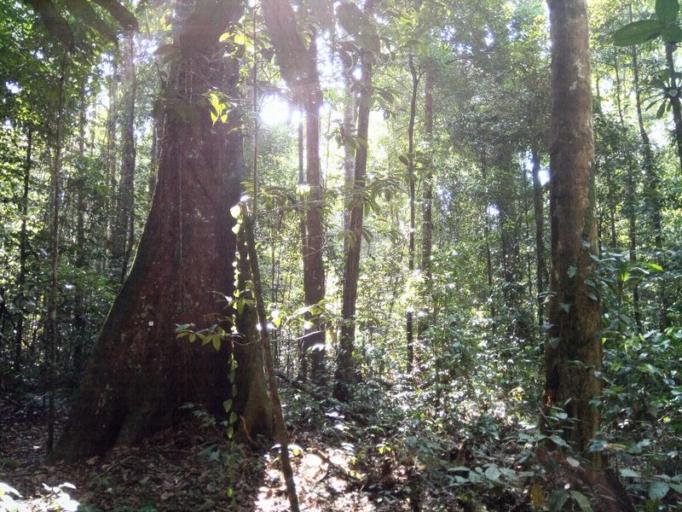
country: SR
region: Brokopondo
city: Brownsweg
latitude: 4.9501
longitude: -55.1869
